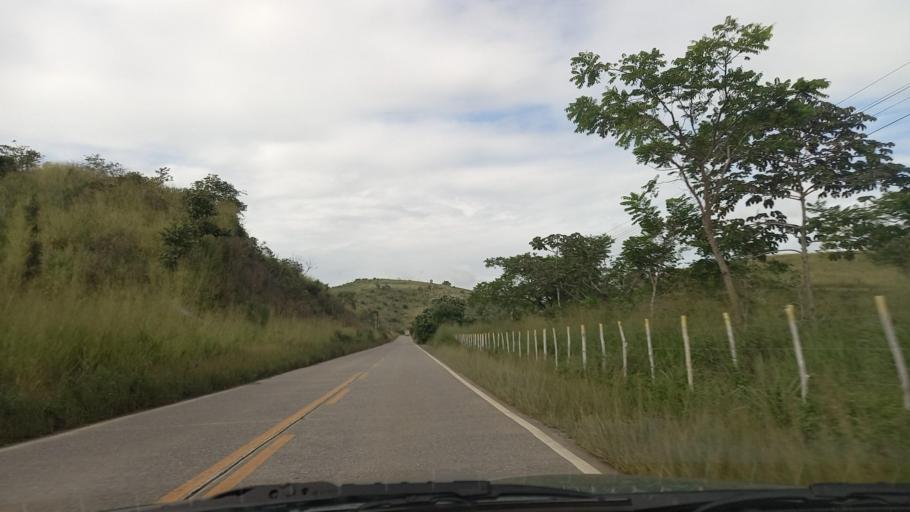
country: BR
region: Pernambuco
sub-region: Catende
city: Catende
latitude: -8.6920
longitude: -35.7124
